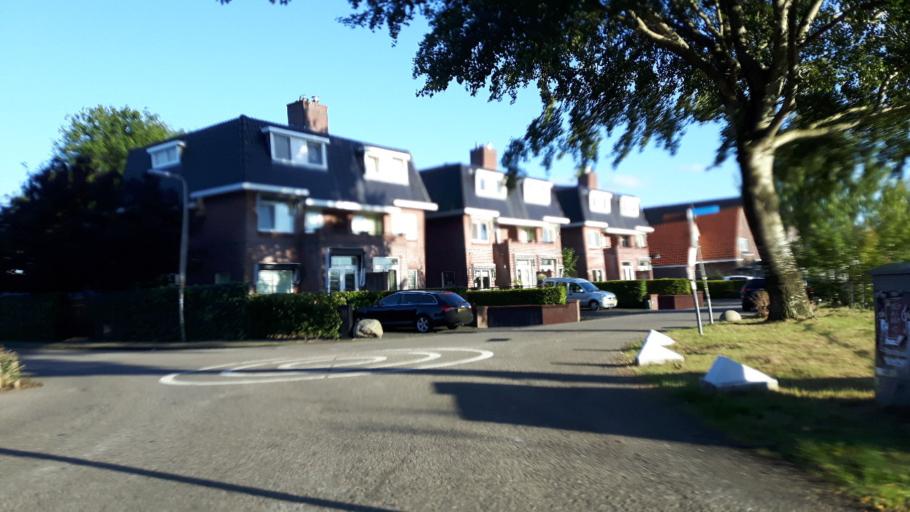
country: NL
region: Utrecht
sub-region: Gemeente Oudewater
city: Oudewater
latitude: 52.0349
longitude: 4.8607
